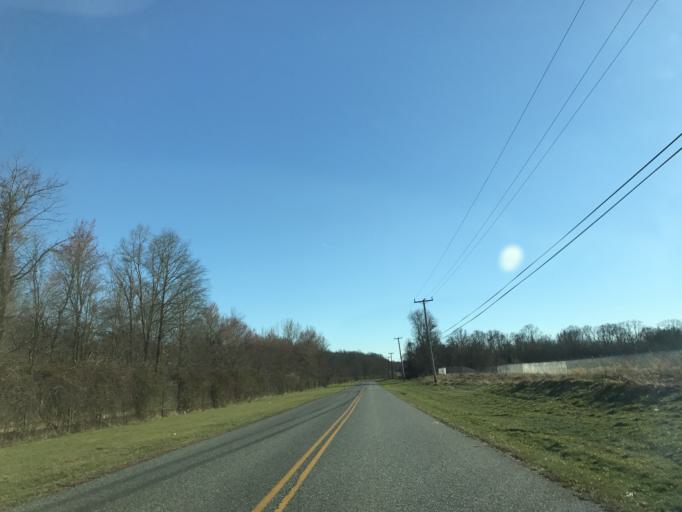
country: US
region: Maryland
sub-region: Harford County
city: Perryman
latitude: 39.4362
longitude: -76.2165
